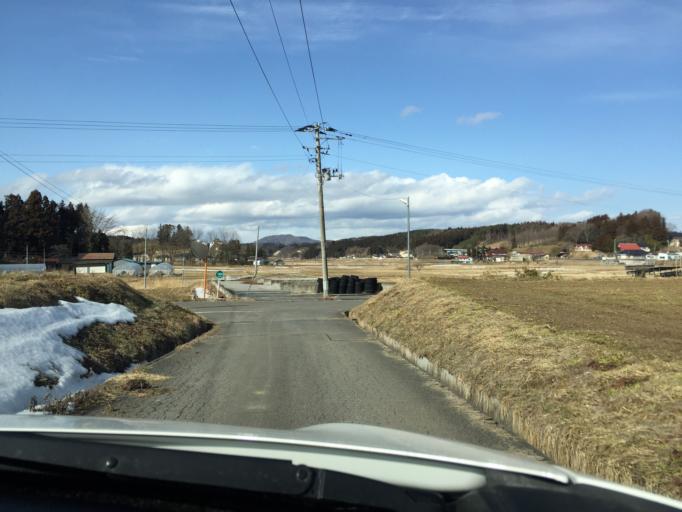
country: JP
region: Fukushima
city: Ishikawa
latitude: 37.2531
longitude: 140.5568
